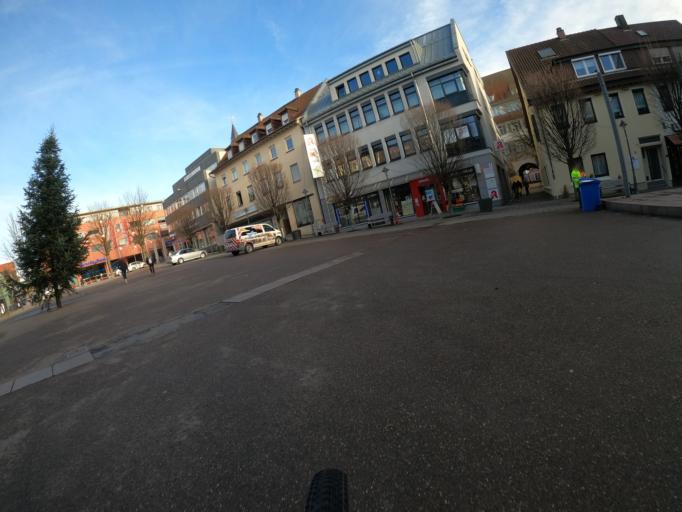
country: DE
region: Baden-Wuerttemberg
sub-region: Regierungsbezirk Stuttgart
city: Goeppingen
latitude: 48.7035
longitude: 9.6498
